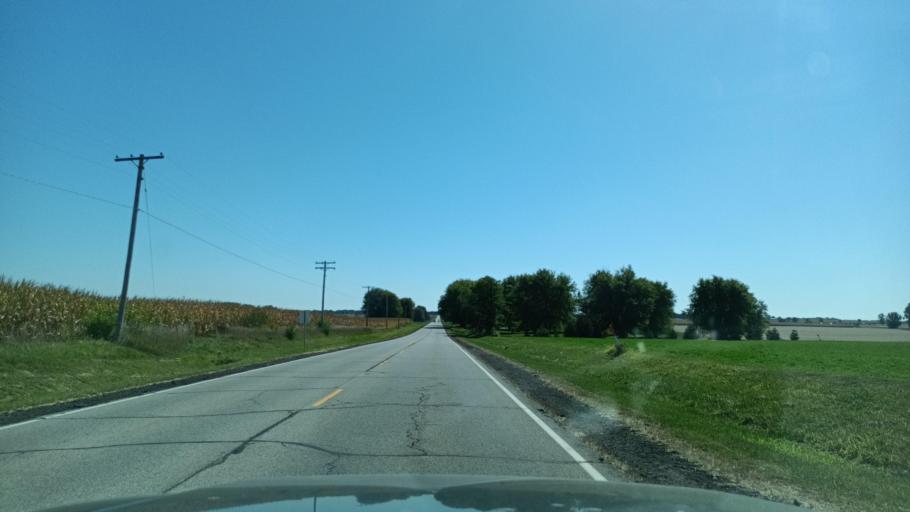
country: US
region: Illinois
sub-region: Peoria County
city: Elmwood
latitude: 40.8297
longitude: -89.8670
